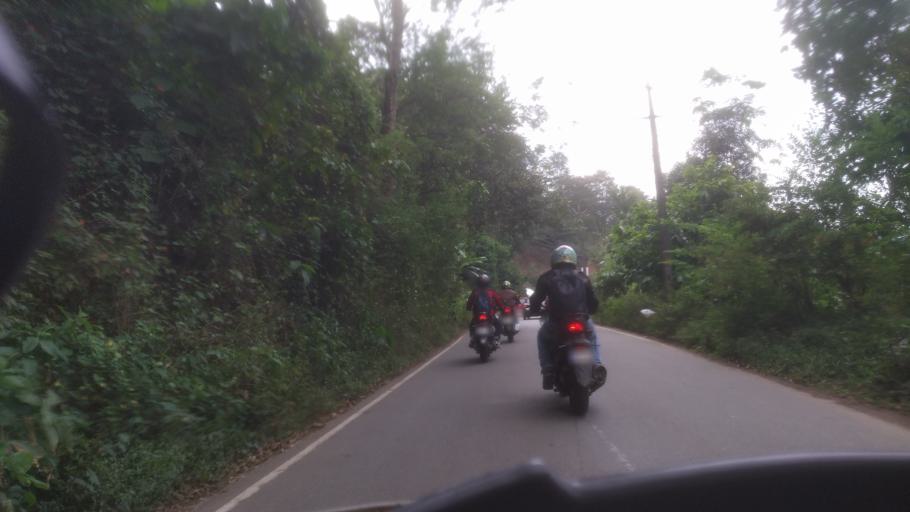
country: IN
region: Kerala
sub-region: Idukki
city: Munnar
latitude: 9.9830
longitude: 76.9912
